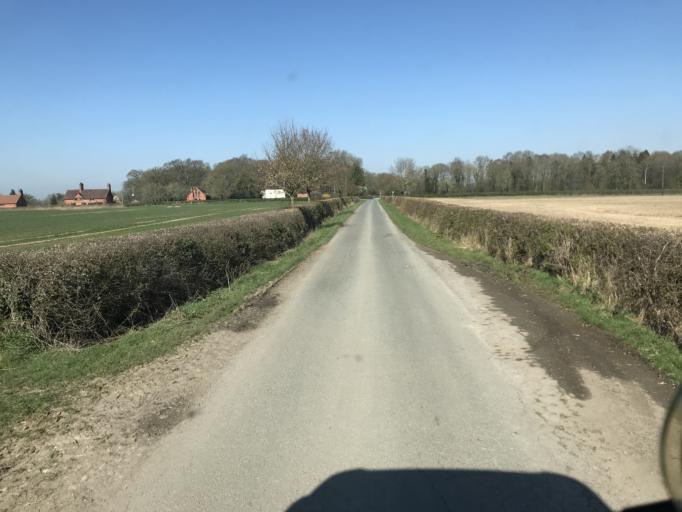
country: GB
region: England
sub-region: Cheshire West and Chester
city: Aldford
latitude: 53.1289
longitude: -2.8591
